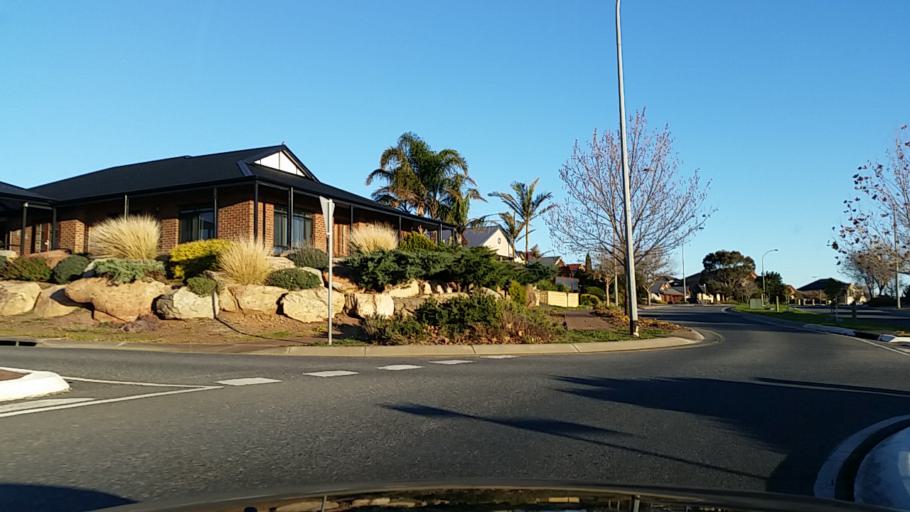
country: AU
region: South Australia
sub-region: Onkaparinga
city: Moana
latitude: -35.2078
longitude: 138.4881
